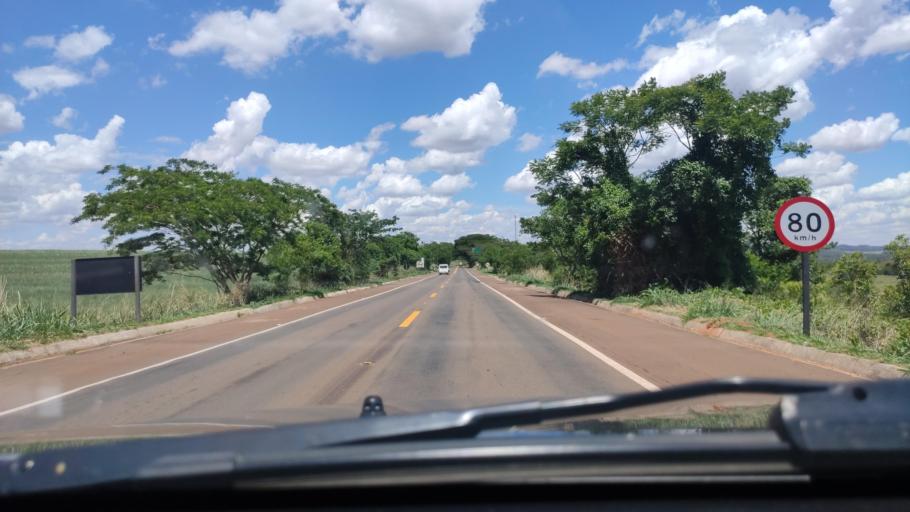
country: BR
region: Sao Paulo
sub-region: Boa Esperanca Do Sul
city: Boa Esperanca do Sul
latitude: -22.0698
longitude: -48.4253
